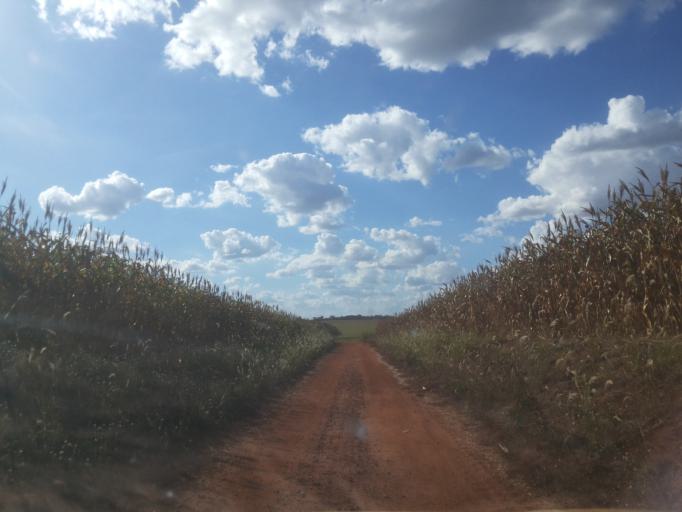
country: BR
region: Minas Gerais
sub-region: Capinopolis
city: Capinopolis
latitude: -18.5885
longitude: -49.4952
